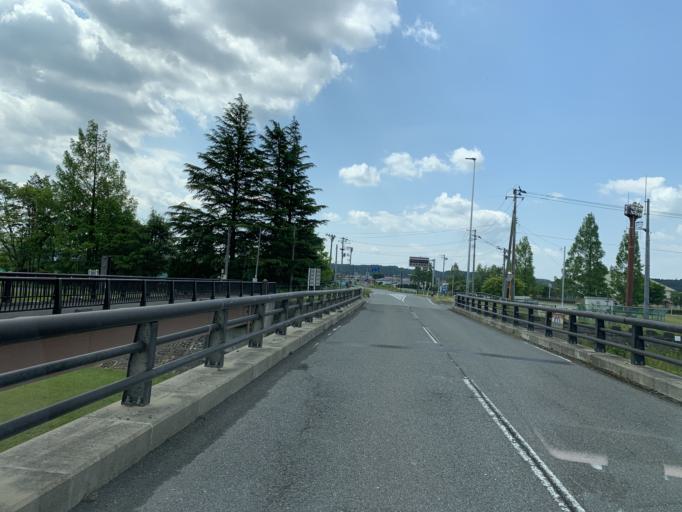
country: JP
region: Miyagi
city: Furukawa
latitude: 38.7457
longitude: 140.9539
